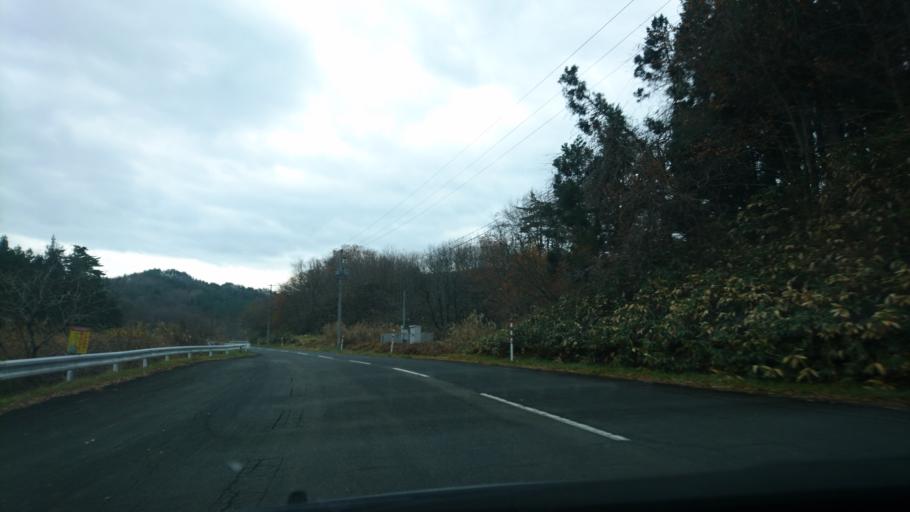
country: JP
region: Iwate
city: Ichinoseki
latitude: 38.9297
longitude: 140.9219
